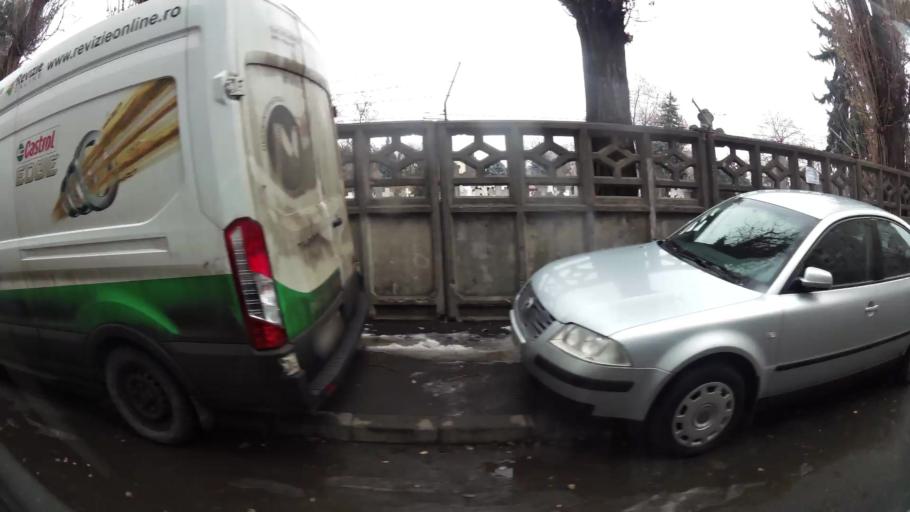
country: RO
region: Bucuresti
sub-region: Municipiul Bucuresti
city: Bucuresti
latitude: 44.4185
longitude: 26.0494
